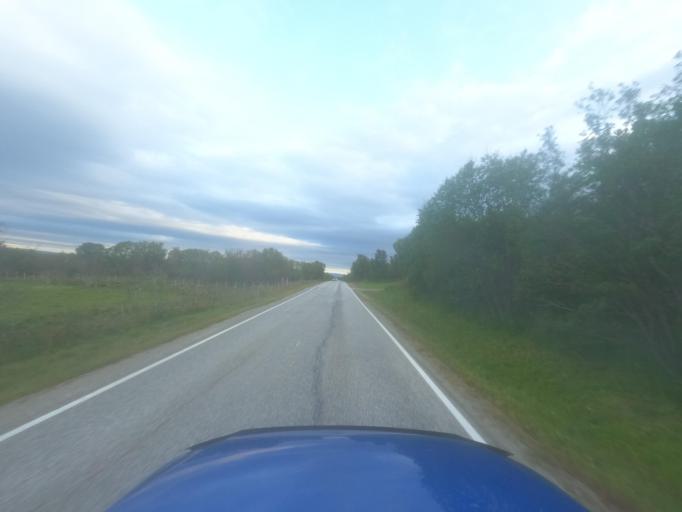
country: NO
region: Finnmark Fylke
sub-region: Porsanger
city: Lakselv
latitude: 70.4691
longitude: 25.2213
